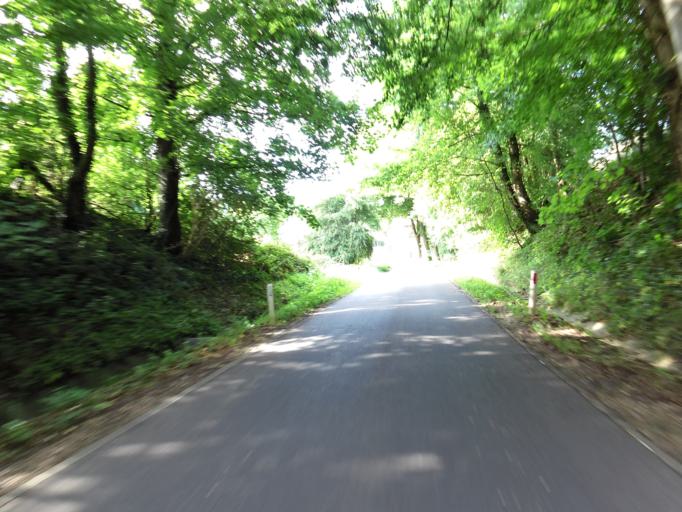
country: NL
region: Limburg
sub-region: Gemeente Nuth
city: Nuth
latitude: 50.9204
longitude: 5.8621
